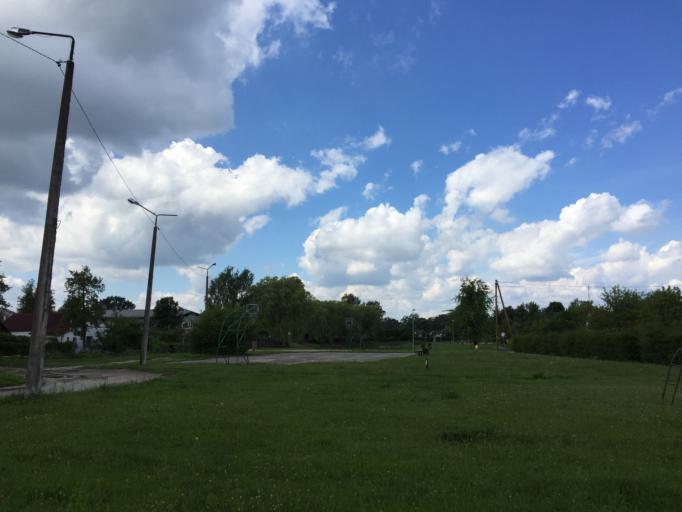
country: LV
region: Ozolnieku
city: Ozolnieki
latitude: 56.6579
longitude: 23.7595
